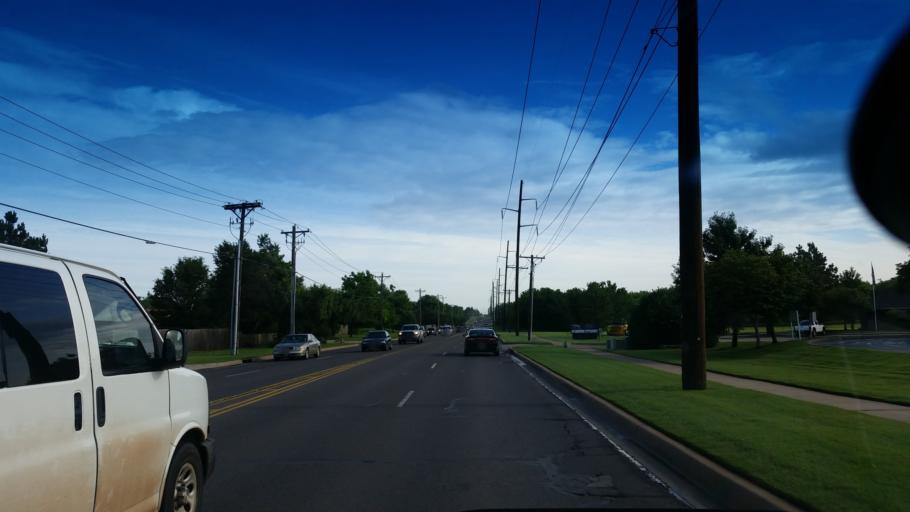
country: US
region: Oklahoma
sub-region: Oklahoma County
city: Edmond
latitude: 35.6399
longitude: -97.5138
